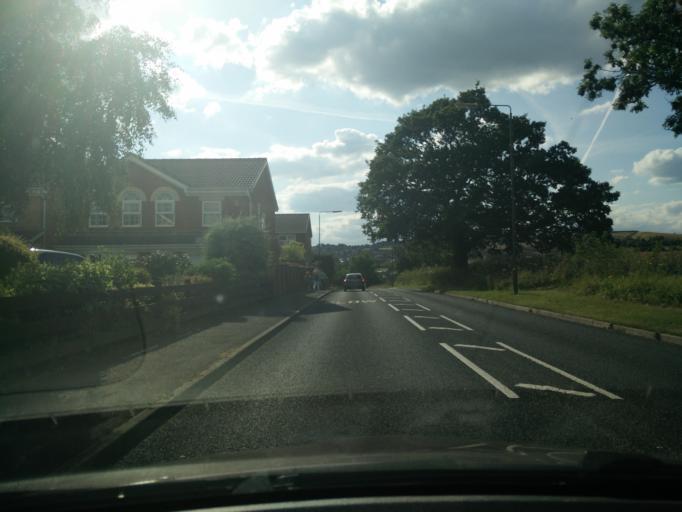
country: GB
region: England
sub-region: Derbyshire
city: Heage
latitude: 53.0314
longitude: -1.4519
